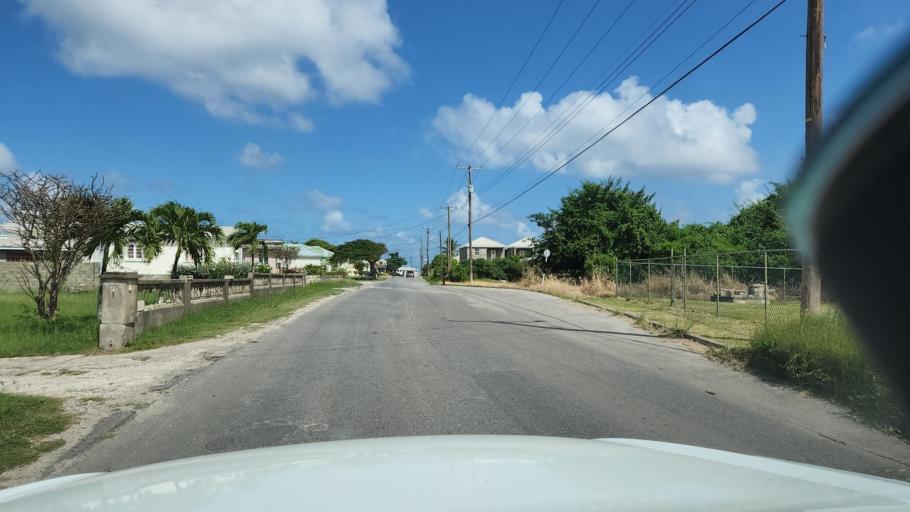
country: BB
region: Saint Philip
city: Crane
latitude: 13.1399
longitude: -59.4334
